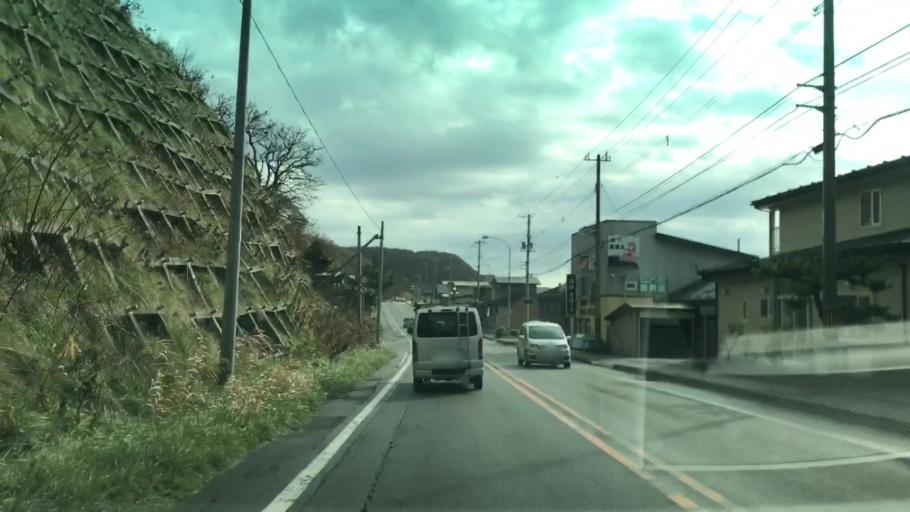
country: JP
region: Hokkaido
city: Shizunai-furukawacho
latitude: 42.1523
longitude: 142.7983
